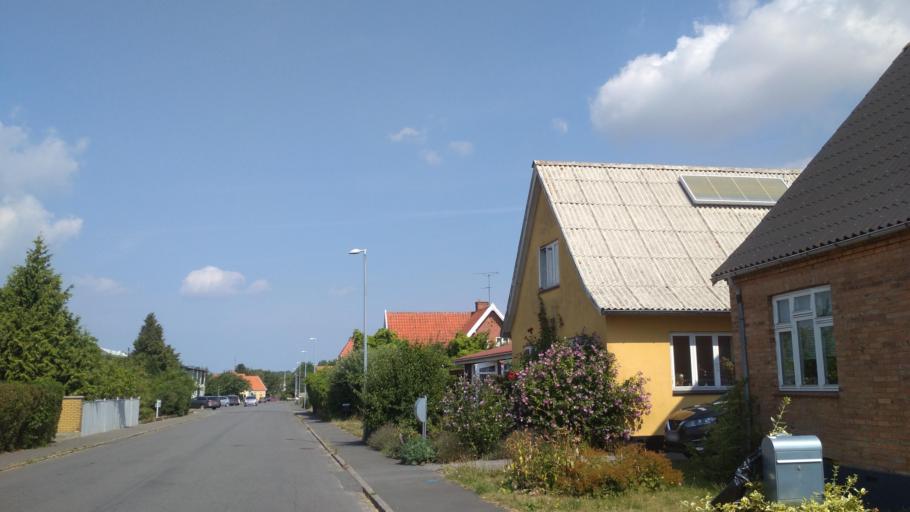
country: DK
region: Capital Region
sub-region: Bornholm Kommune
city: Akirkeby
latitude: 55.0689
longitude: 14.9269
